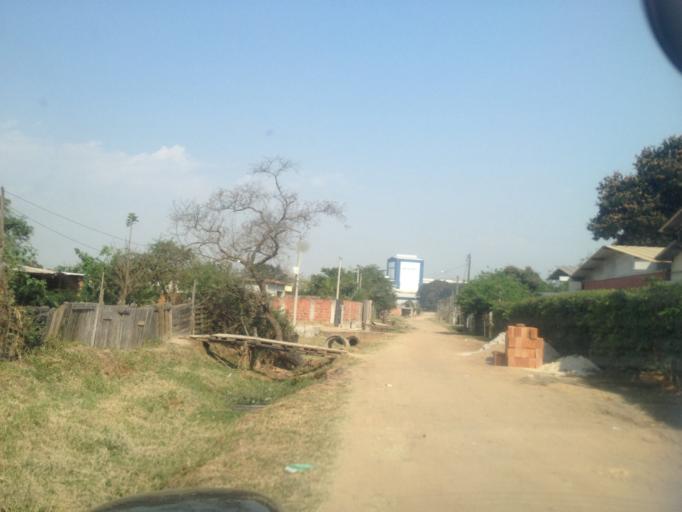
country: BR
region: Rio de Janeiro
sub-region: Porto Real
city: Porto Real
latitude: -22.4317
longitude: -44.3390
